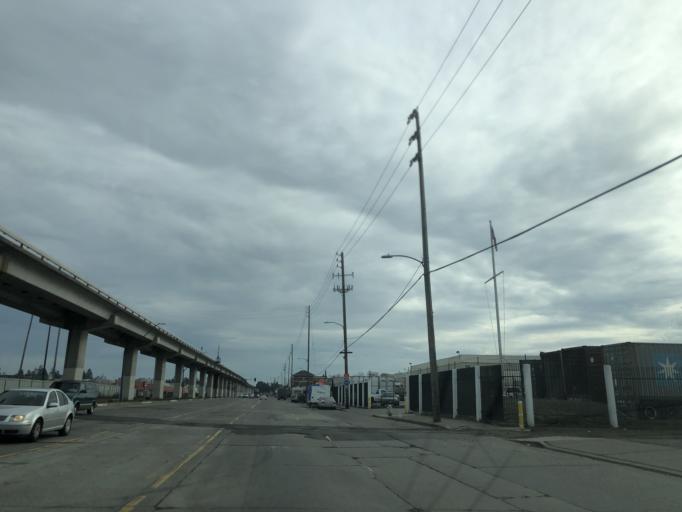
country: US
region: California
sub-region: Alameda County
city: San Leandro
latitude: 37.7409
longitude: -122.1819
